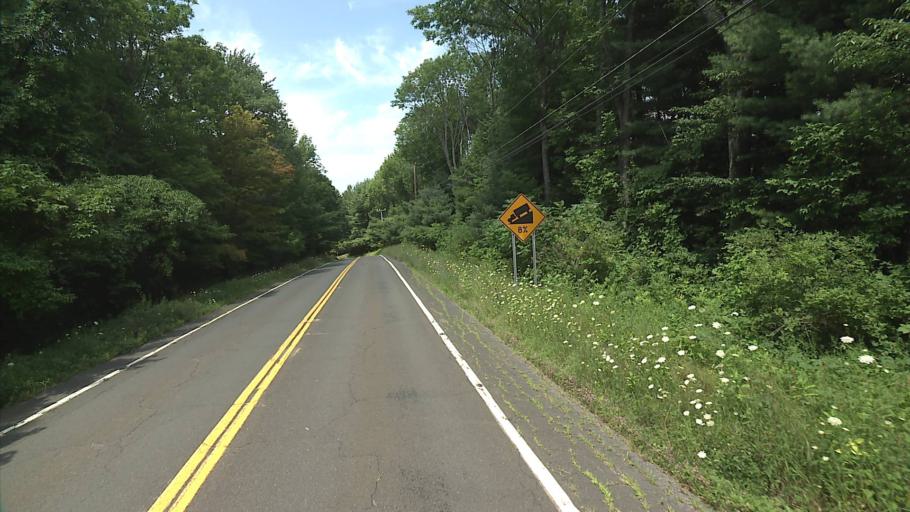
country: US
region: Connecticut
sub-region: Litchfield County
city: Winsted
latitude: 41.9831
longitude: -73.1110
